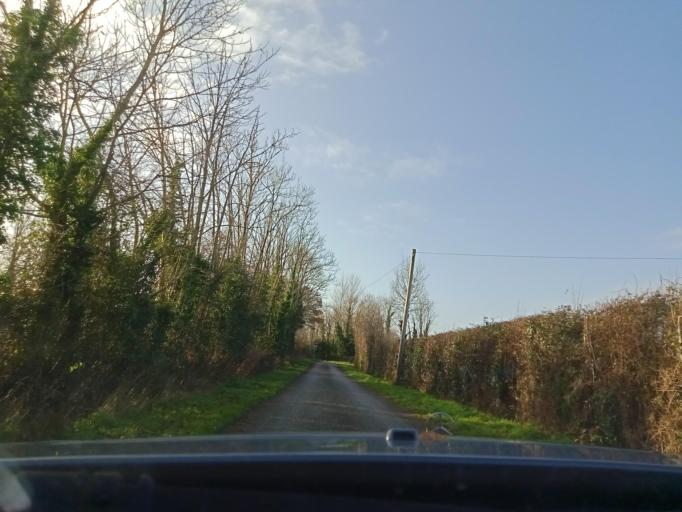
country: IE
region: Leinster
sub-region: Kilkenny
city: Callan
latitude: 52.5231
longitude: -7.3997
